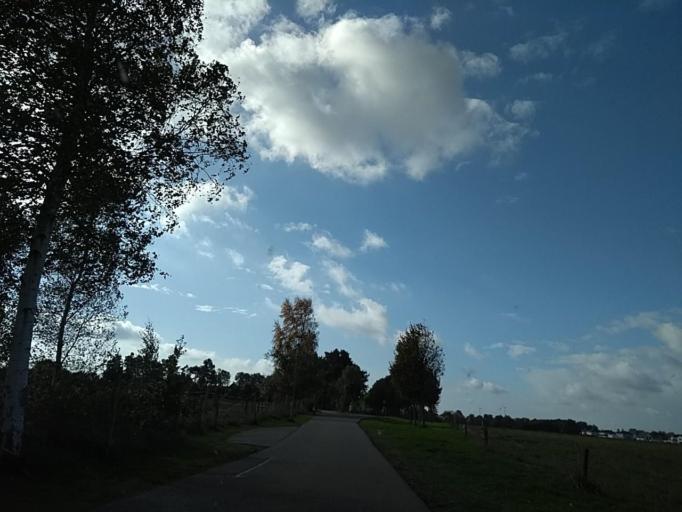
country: DE
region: Mecklenburg-Vorpommern
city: Rovershagen
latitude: 54.1824
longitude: 12.2446
